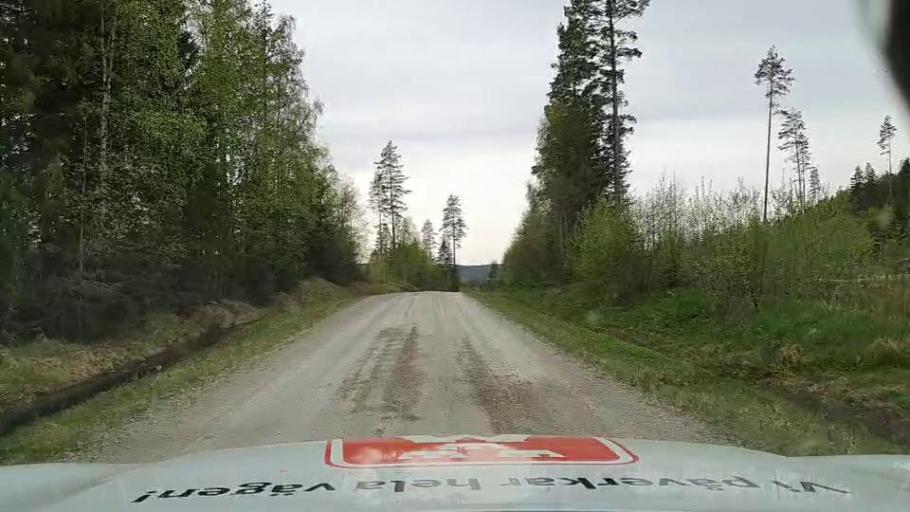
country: SE
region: Jaemtland
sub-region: Bergs Kommun
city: Hoverberg
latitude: 62.6779
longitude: 14.7582
